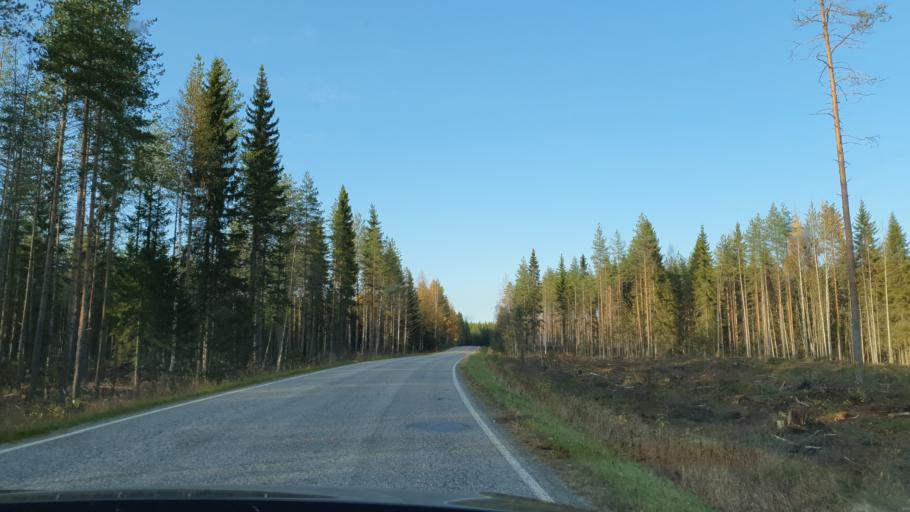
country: FI
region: Kainuu
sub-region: Kehys-Kainuu
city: Kuhmo
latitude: 64.1862
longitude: 29.4445
